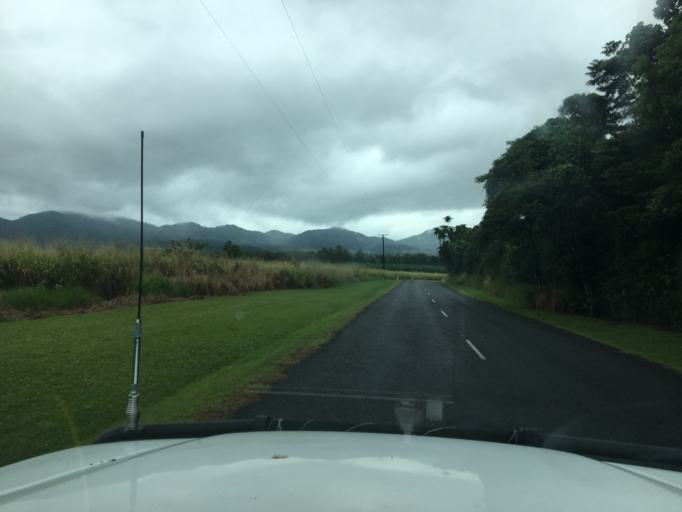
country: AU
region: Queensland
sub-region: Cassowary Coast
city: Innisfail
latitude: -17.4399
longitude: 145.8606
